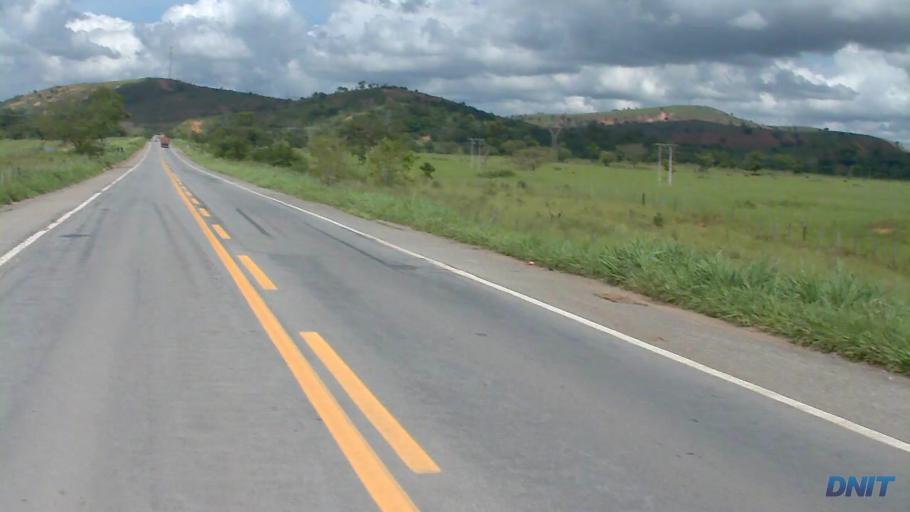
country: BR
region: Minas Gerais
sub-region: Governador Valadares
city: Governador Valadares
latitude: -19.0127
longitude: -42.1394
